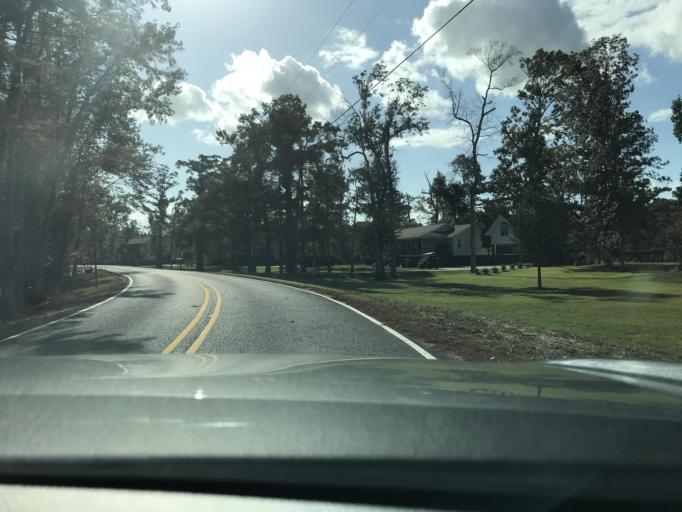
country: US
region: Louisiana
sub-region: Calcasieu Parish
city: Westlake
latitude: 30.3196
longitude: -93.2943
